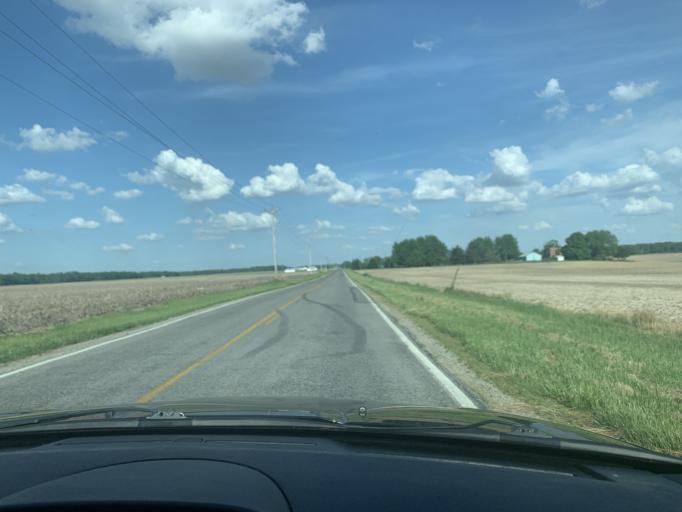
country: US
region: Ohio
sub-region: Logan County
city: De Graff
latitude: 40.2442
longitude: -84.0171
